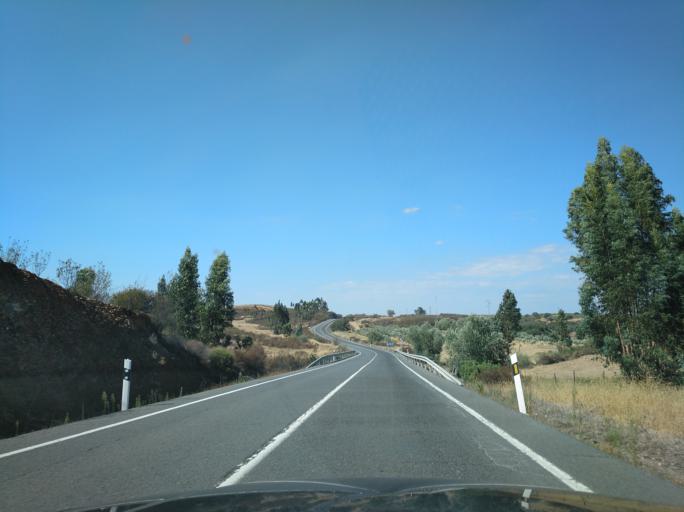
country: ES
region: Andalusia
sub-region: Provincia de Huelva
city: San Bartolome de la Torre
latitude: 37.4904
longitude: -7.1325
